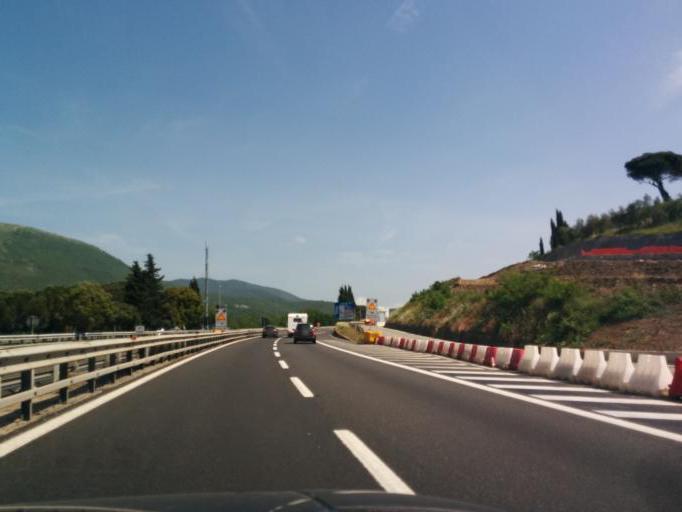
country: IT
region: Tuscany
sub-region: Province of Florence
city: Carraia
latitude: 43.8880
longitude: 11.1843
